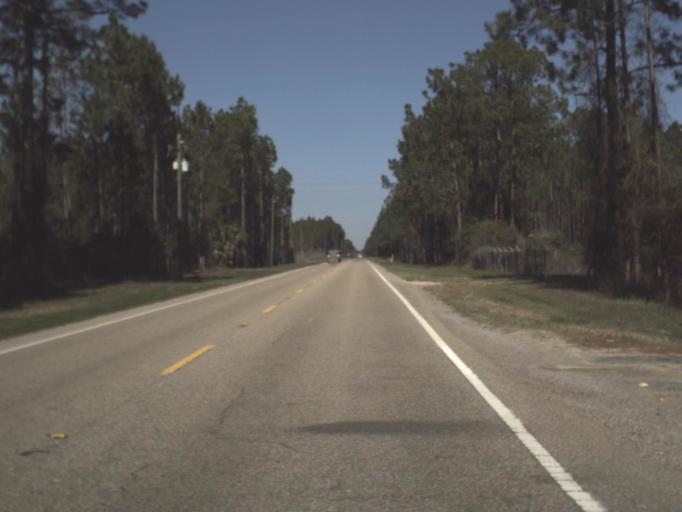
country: US
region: Florida
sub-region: Gulf County
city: Port Saint Joe
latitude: 29.8492
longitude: -85.2589
